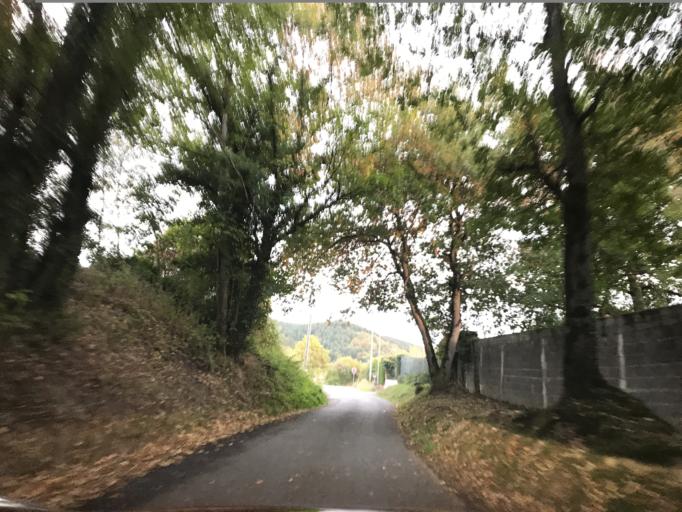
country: FR
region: Auvergne
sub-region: Departement du Puy-de-Dome
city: Thiers
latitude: 45.8425
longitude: 3.5430
